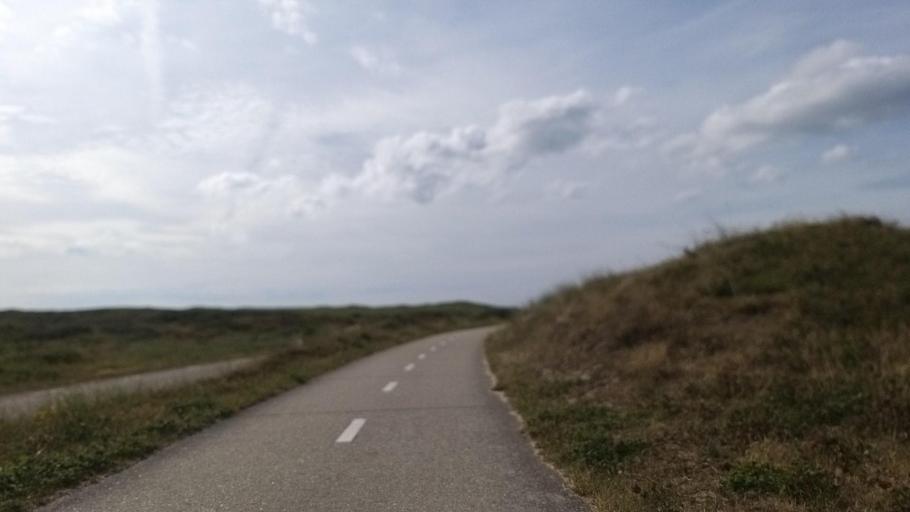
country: NL
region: North Holland
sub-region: Gemeente Texel
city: Den Burg
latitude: 53.1599
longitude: 4.8262
